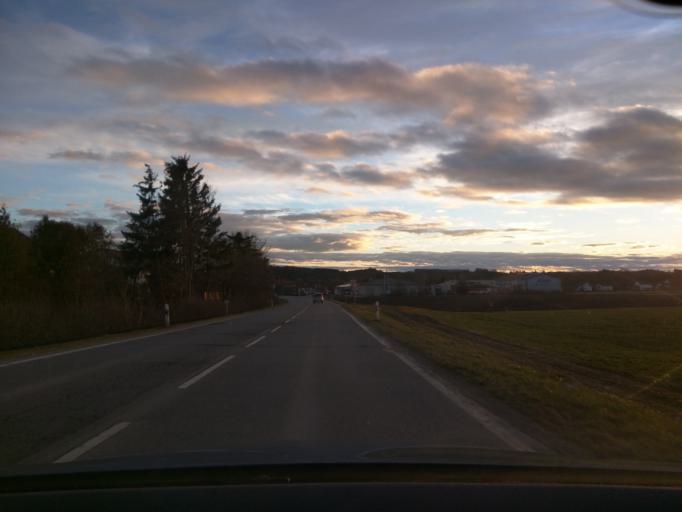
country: DE
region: Bavaria
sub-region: Upper Bavaria
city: Zolling
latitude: 48.4540
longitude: 11.7669
